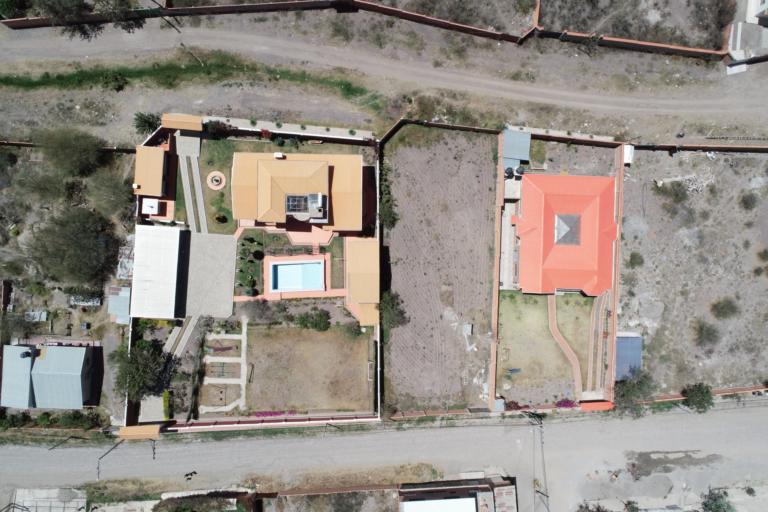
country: BO
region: La Paz
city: La Paz
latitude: -16.6421
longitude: -68.0438
